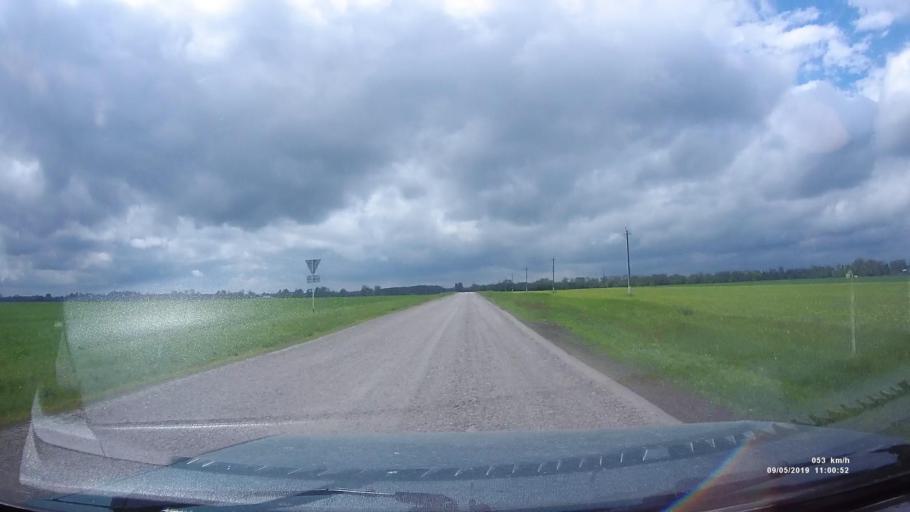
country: RU
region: Rostov
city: Peshkovo
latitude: 46.8513
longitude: 39.2166
